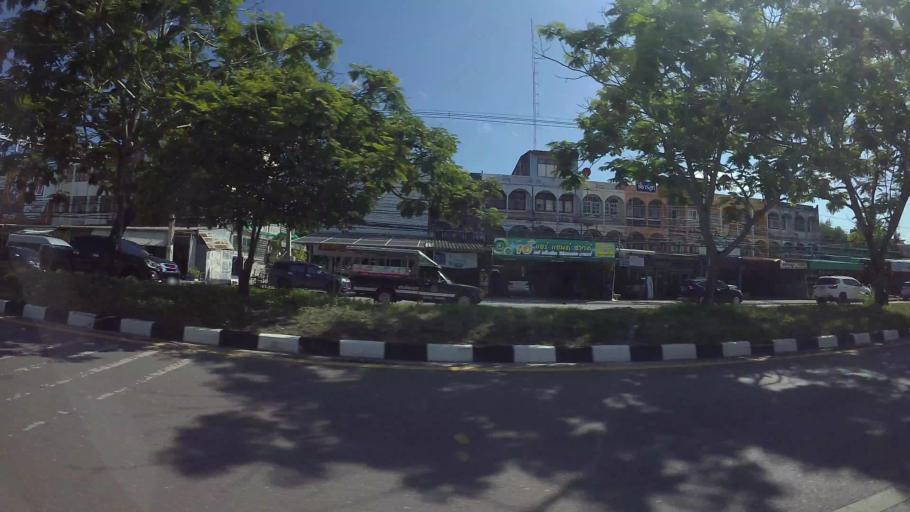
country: TH
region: Rayong
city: Rayong
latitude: 12.6714
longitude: 101.2929
